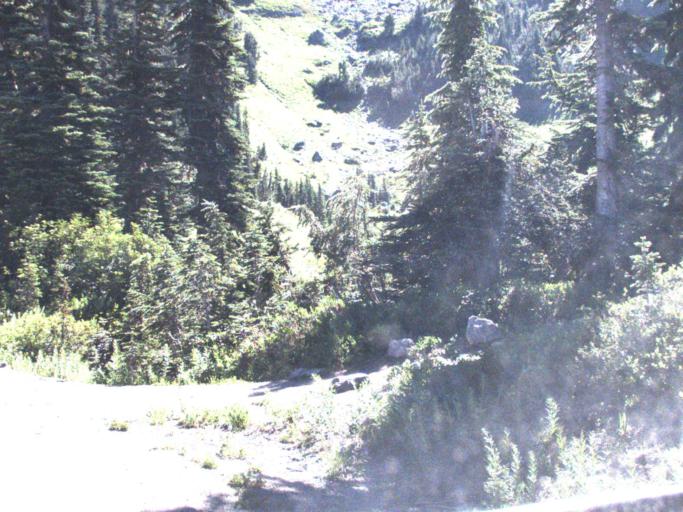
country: US
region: Washington
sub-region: King County
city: Enumclaw
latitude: 46.8677
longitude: -121.5156
